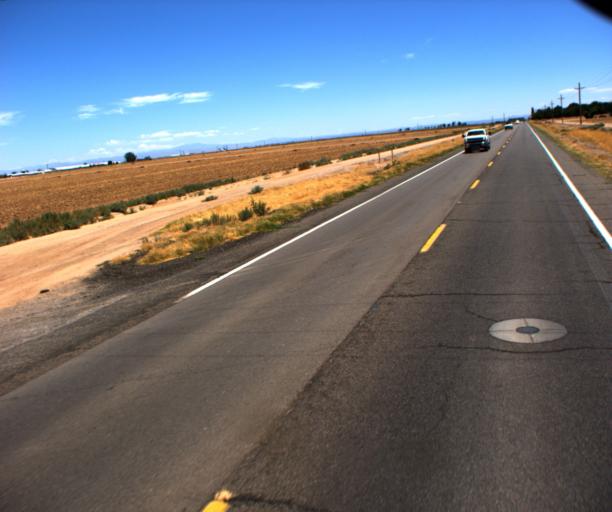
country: US
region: Arizona
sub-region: Pinal County
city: Casa Grande
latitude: 32.8797
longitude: -111.6625
